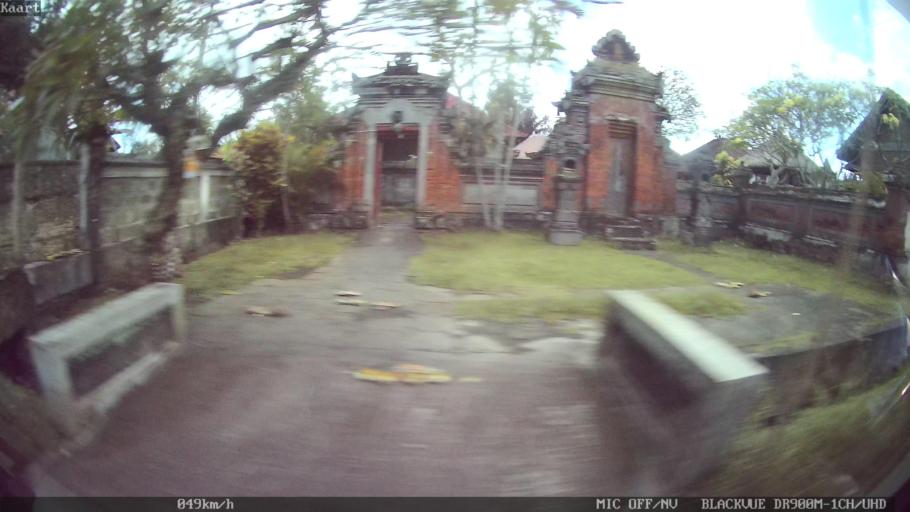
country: ID
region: Bali
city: Banjar Sedang
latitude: -8.5604
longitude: 115.2865
